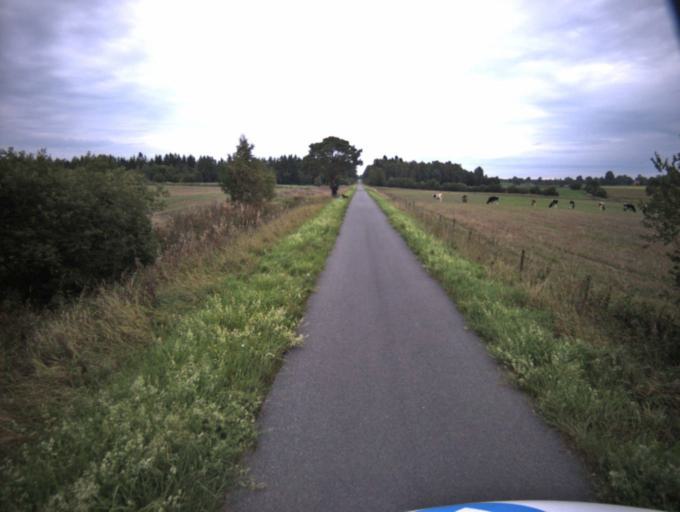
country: SE
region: Vaestra Goetaland
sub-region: Ulricehamns Kommun
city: Ulricehamn
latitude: 57.9577
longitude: 13.5105
